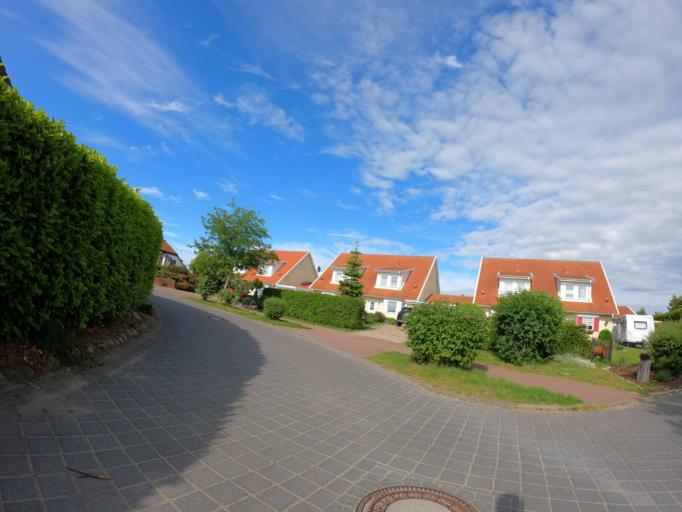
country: DE
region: Mecklenburg-Vorpommern
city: Prohn
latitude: 54.3500
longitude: 13.0148
